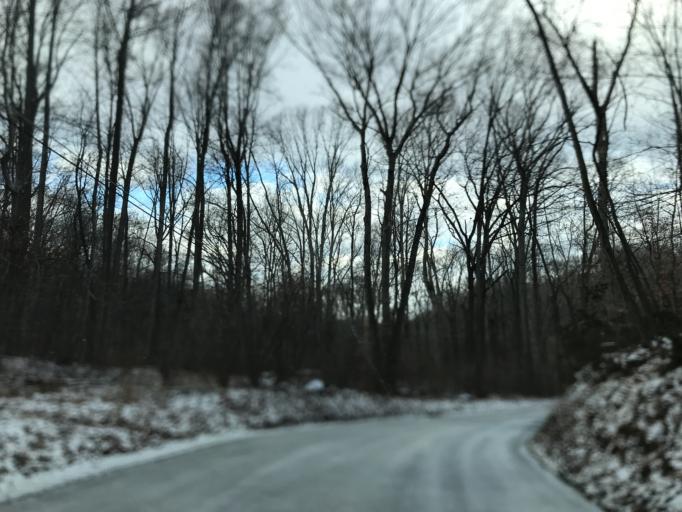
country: US
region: Maryland
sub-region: Baltimore County
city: Hunt Valley
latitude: 39.5933
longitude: -76.6301
